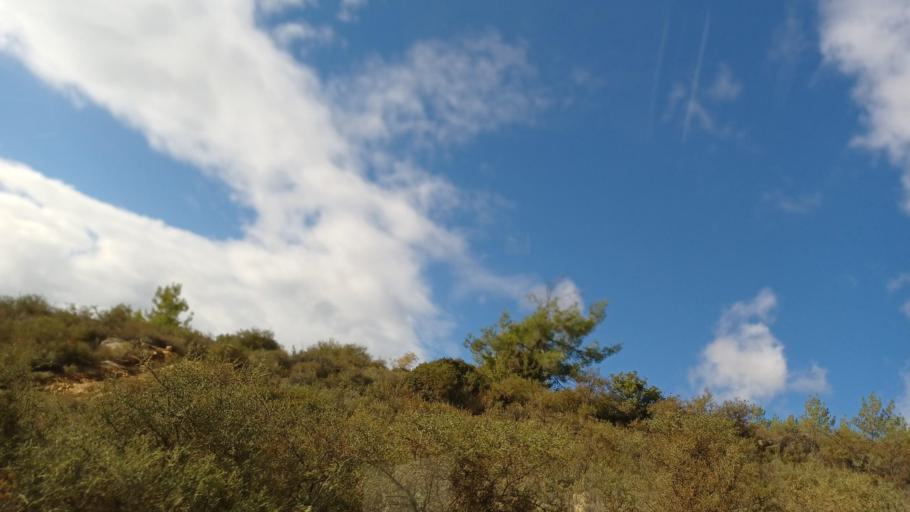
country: CY
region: Limassol
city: Sotira
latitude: 34.7510
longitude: 32.8611
